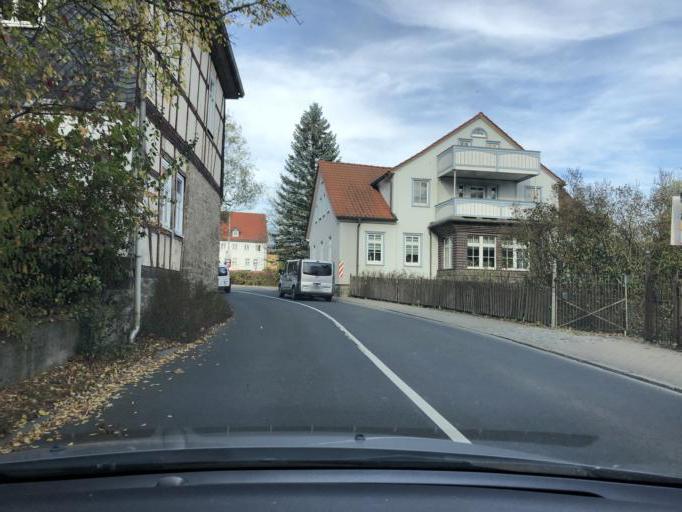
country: DE
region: Thuringia
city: Hildburghausen
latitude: 50.4262
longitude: 10.7334
